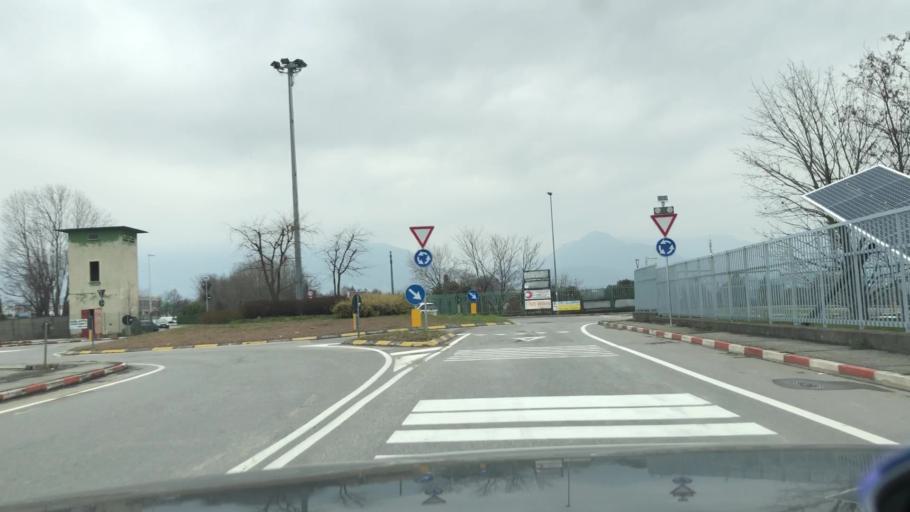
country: IT
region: Lombardy
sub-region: Provincia di Bergamo
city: Ponte San Pietro
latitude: 45.7079
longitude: 9.5838
